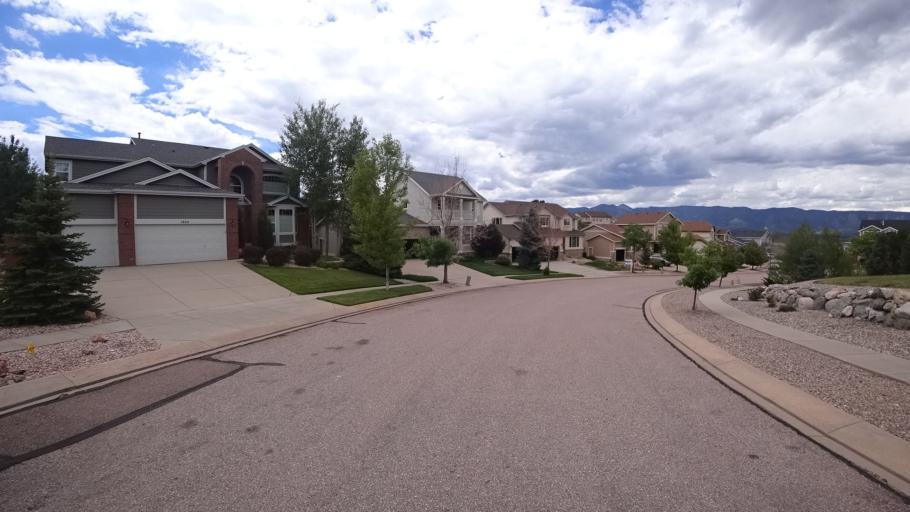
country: US
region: Colorado
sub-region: El Paso County
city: Gleneagle
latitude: 39.0326
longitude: -104.8099
